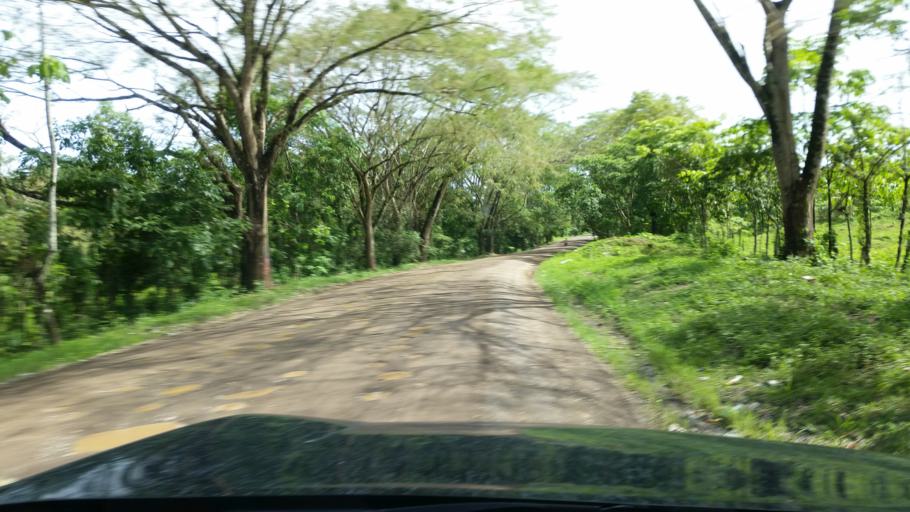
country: NI
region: Atlantico Norte (RAAN)
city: Siuna
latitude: 13.7052
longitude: -84.7779
